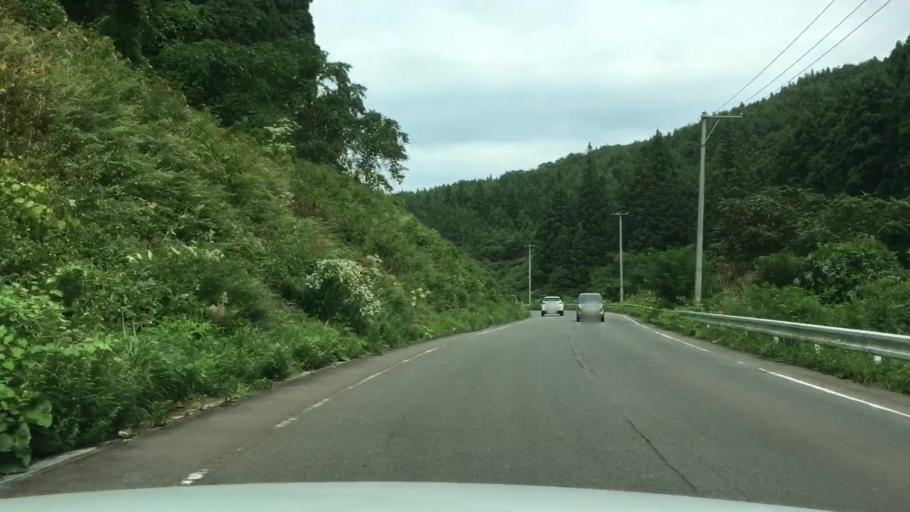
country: JP
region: Aomori
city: Shimokizukuri
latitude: 40.7404
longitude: 140.2448
